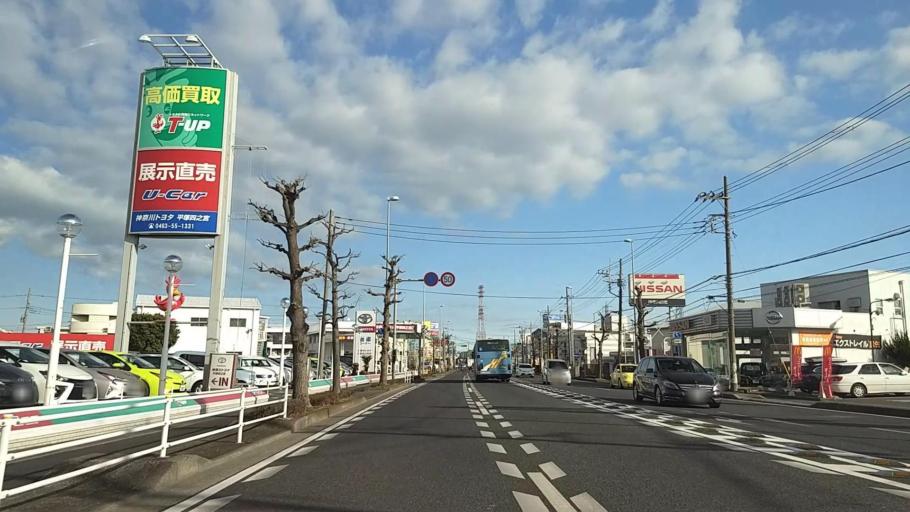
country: JP
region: Kanagawa
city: Hiratsuka
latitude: 35.3605
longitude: 139.3592
